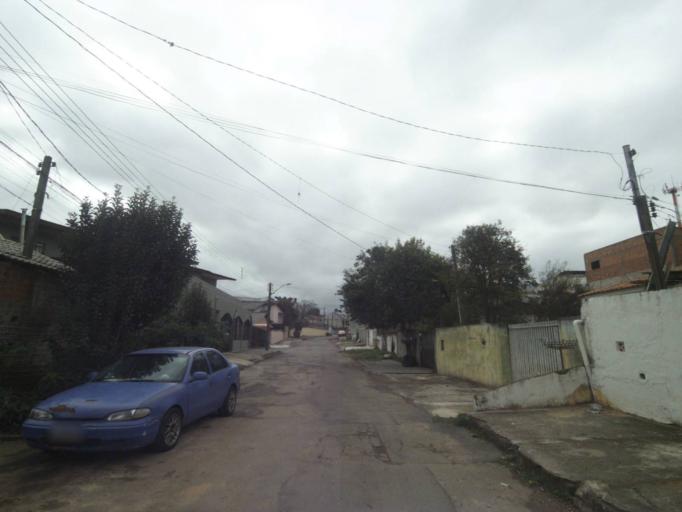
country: BR
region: Parana
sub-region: Sao Jose Dos Pinhais
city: Sao Jose dos Pinhais
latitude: -25.5386
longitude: -49.3010
